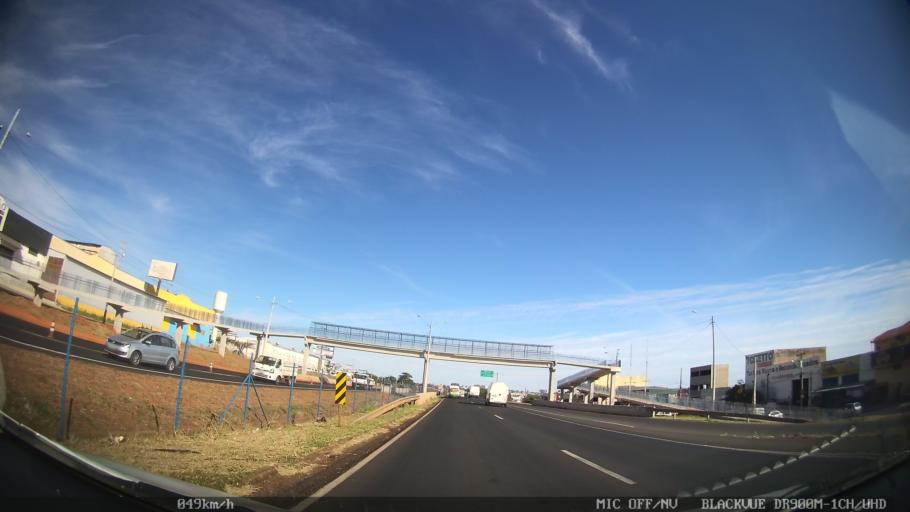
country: BR
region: Sao Paulo
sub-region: Sao Jose Do Rio Preto
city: Sao Jose do Rio Preto
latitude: -20.7977
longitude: -49.3553
